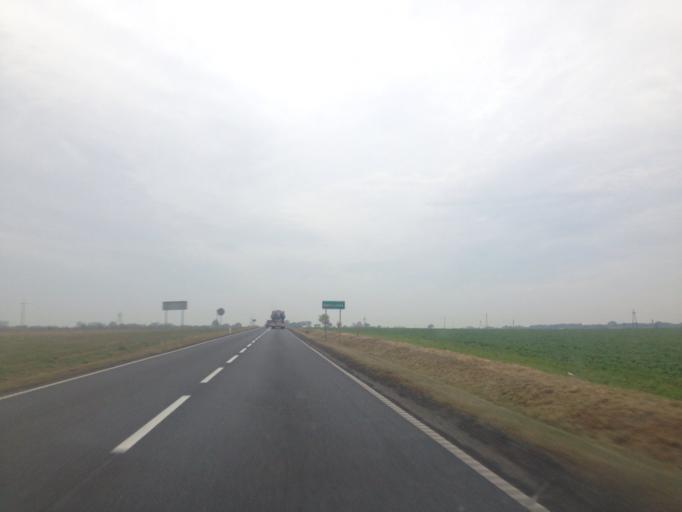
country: PL
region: Kujawsko-Pomorskie
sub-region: Powiat mogilenski
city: Mogilno
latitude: 52.6200
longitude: 18.0341
